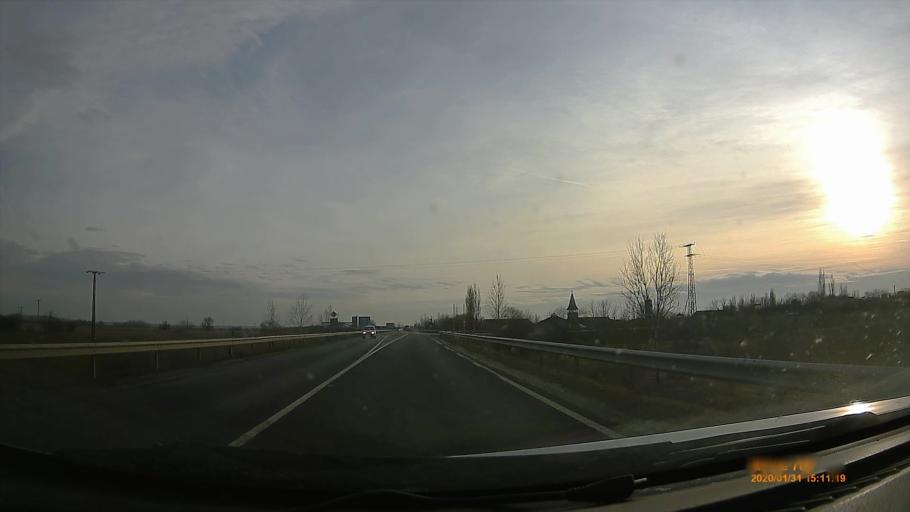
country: HU
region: Hajdu-Bihar
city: Polgar
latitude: 47.8495
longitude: 21.1510
